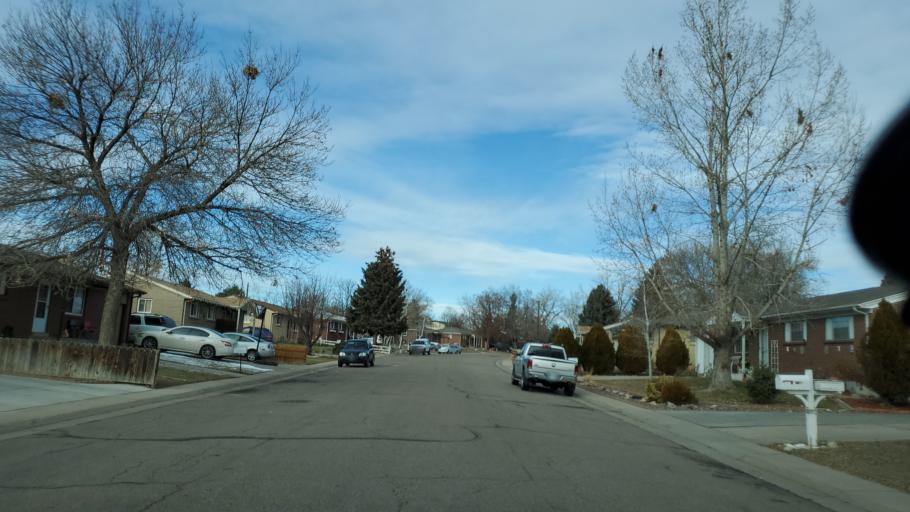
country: US
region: Colorado
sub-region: Adams County
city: Northglenn
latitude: 39.9107
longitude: -104.9612
